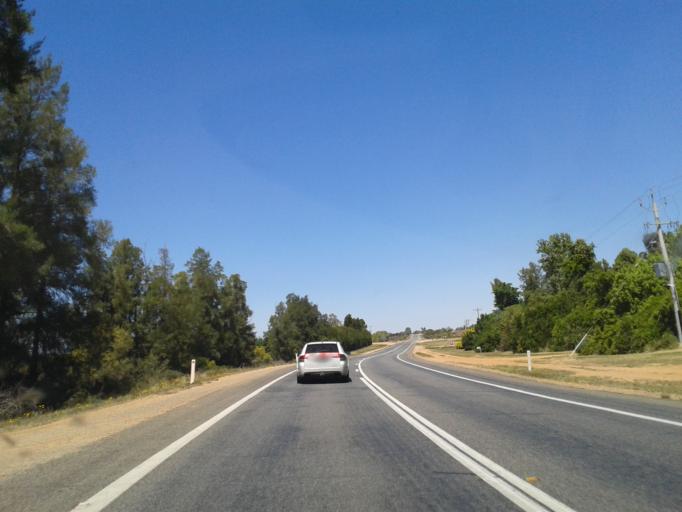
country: AU
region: New South Wales
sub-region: Wentworth
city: Gol Gol
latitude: -34.2088
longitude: 142.2489
